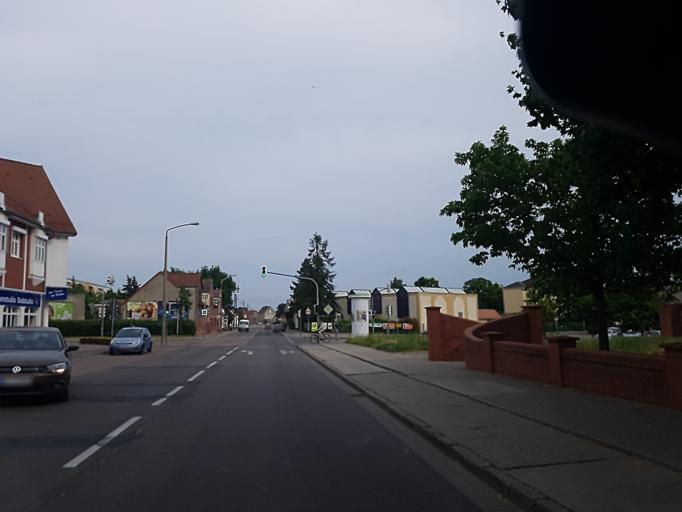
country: DE
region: Saxony-Anhalt
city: Wittenburg
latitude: 51.8787
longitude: 12.6644
